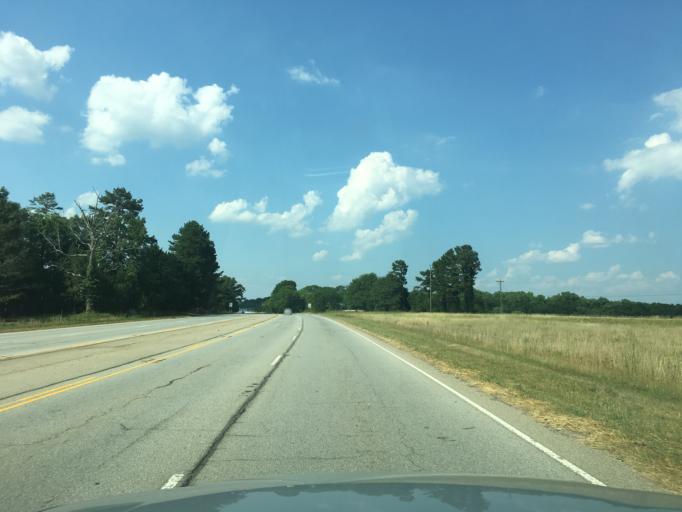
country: US
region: South Carolina
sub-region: Anderson County
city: Northlake
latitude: 34.6039
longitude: -82.6124
